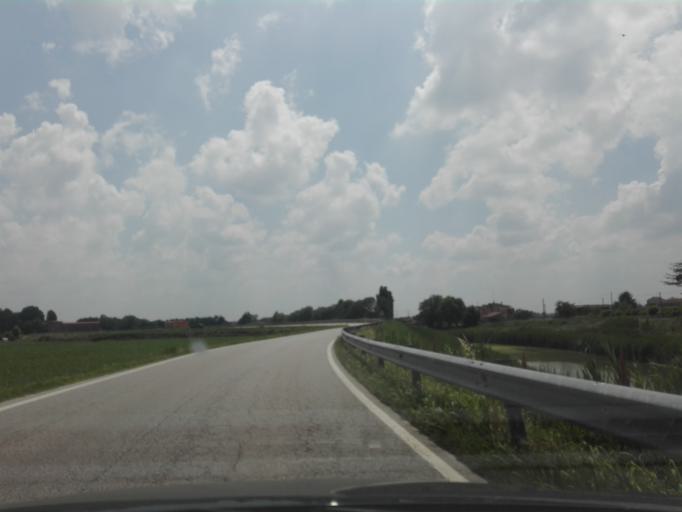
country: IT
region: Veneto
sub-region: Provincia di Rovigo
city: Adria
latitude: 45.0549
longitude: 12.0206
